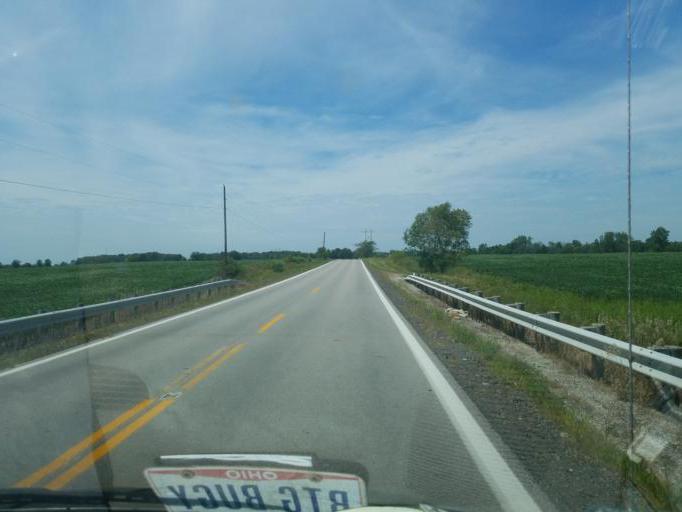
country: US
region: Ohio
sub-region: Madison County
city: West Jefferson
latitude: 39.8625
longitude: -83.2550
